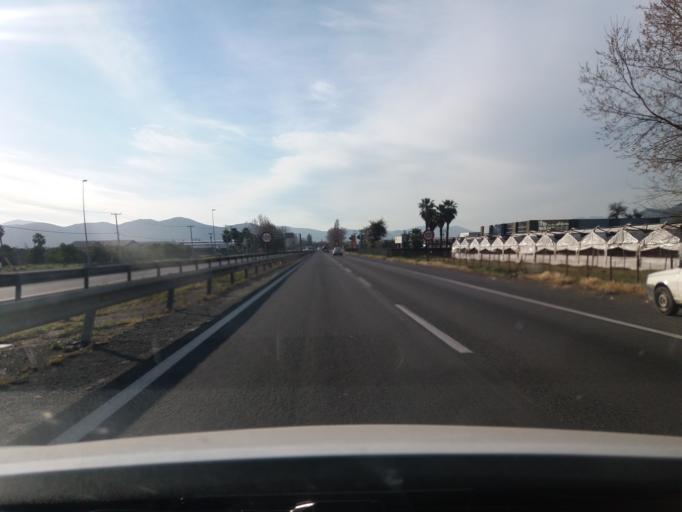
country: CL
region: Valparaiso
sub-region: Provincia de Quillota
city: Hacienda La Calera
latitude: -32.7977
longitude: -71.1585
